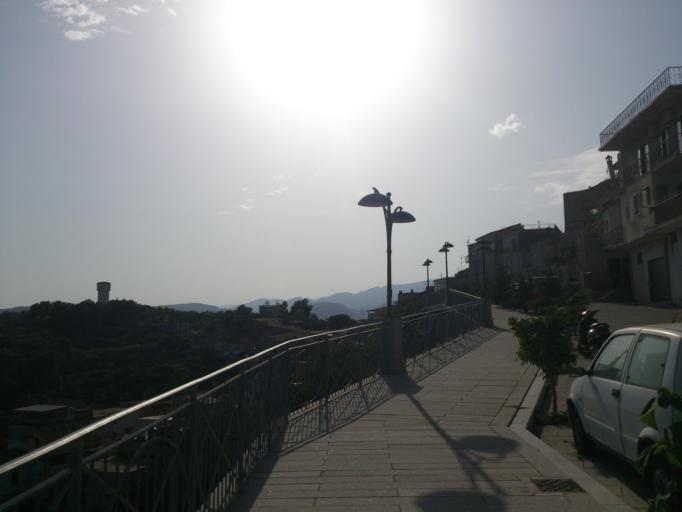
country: IT
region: Calabria
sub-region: Provincia di Reggio Calabria
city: Monasterace
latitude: 38.4532
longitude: 16.5540
